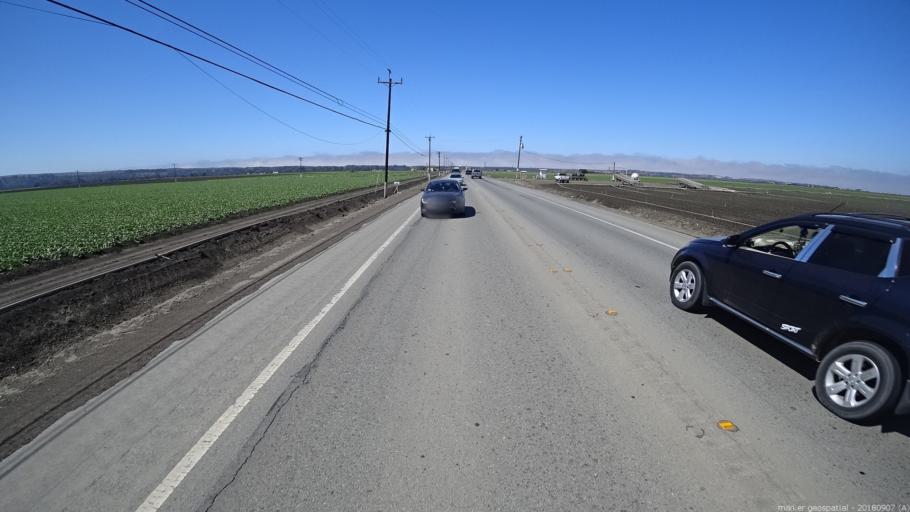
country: US
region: California
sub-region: Monterey County
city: Boronda
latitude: 36.6787
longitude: -121.7180
